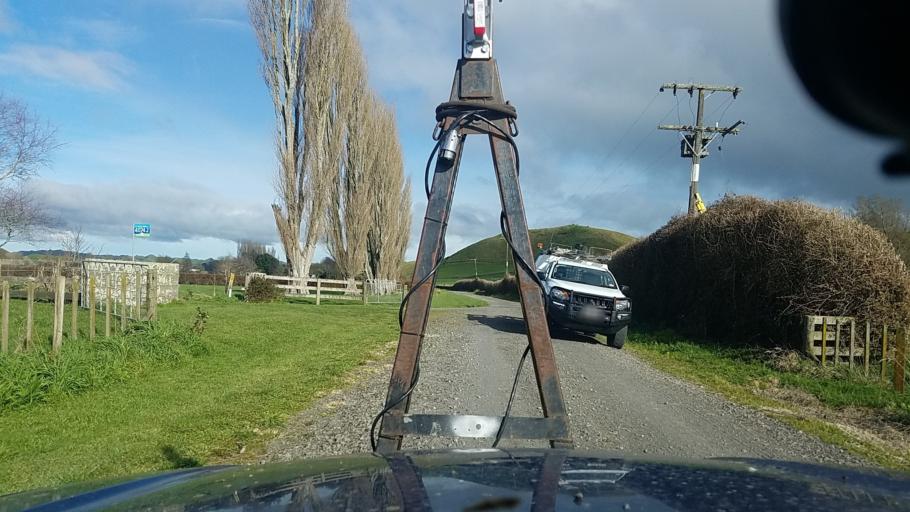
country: NZ
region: Taranaki
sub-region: South Taranaki District
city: Eltham
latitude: -39.3353
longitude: 174.4283
